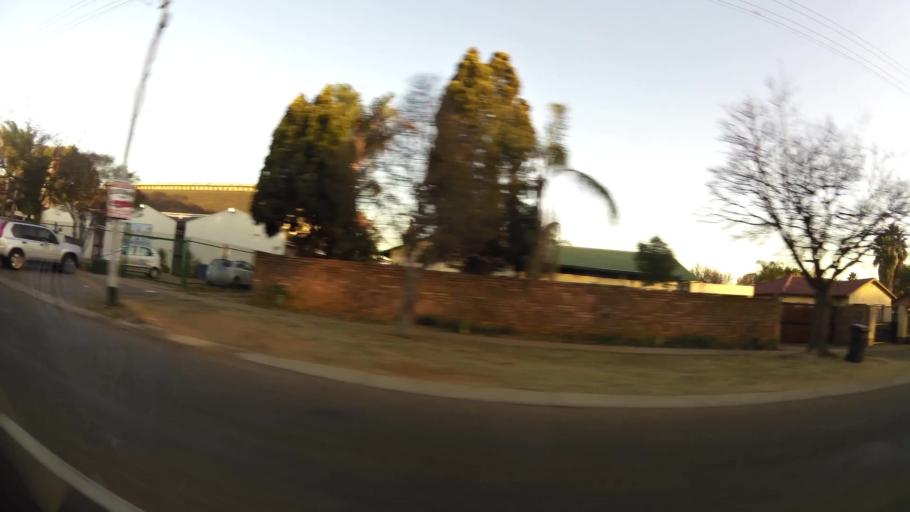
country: ZA
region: Gauteng
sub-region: City of Tshwane Metropolitan Municipality
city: Pretoria
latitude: -25.7115
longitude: 28.2469
